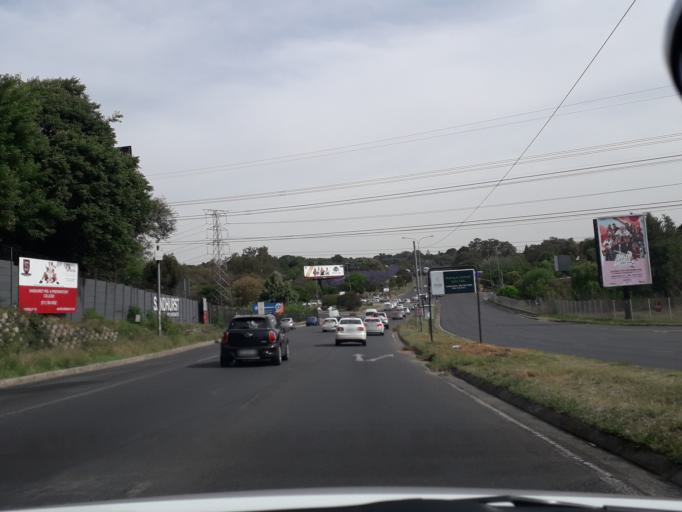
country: ZA
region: Gauteng
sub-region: City of Johannesburg Metropolitan Municipality
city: Johannesburg
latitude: -26.0977
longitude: 28.0322
